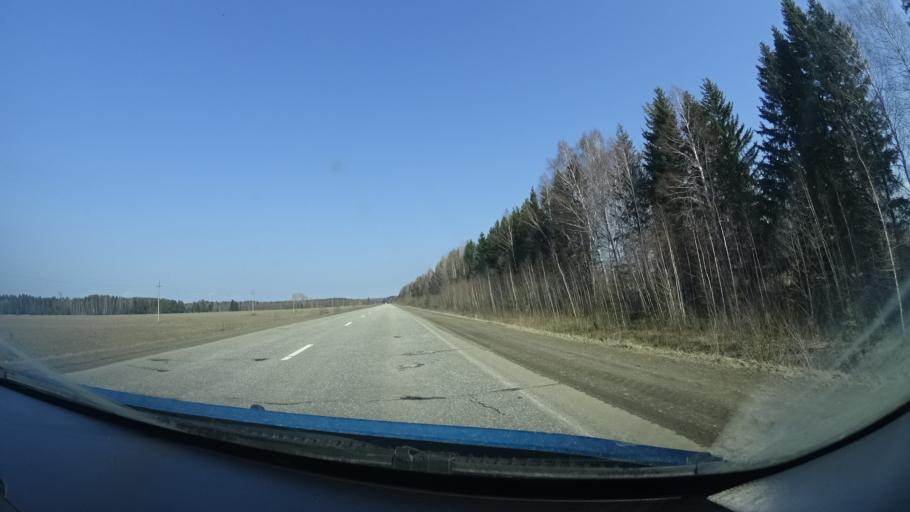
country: RU
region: Perm
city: Osa
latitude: 57.3434
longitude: 55.5901
